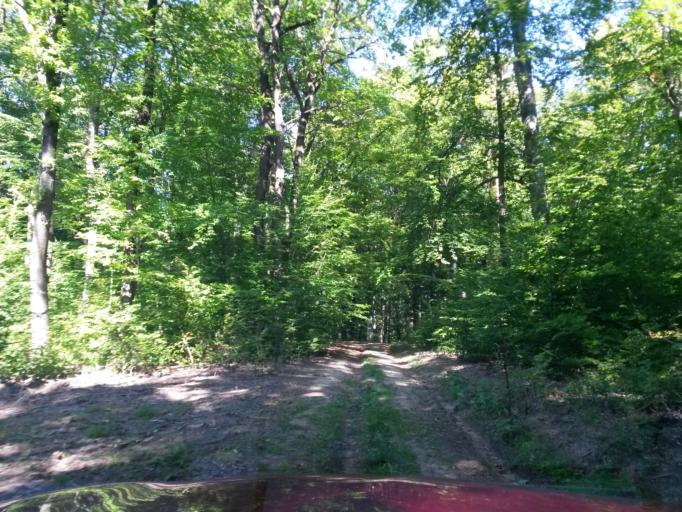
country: SK
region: Presovsky
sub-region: Okres Presov
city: Presov
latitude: 48.9750
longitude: 21.1484
